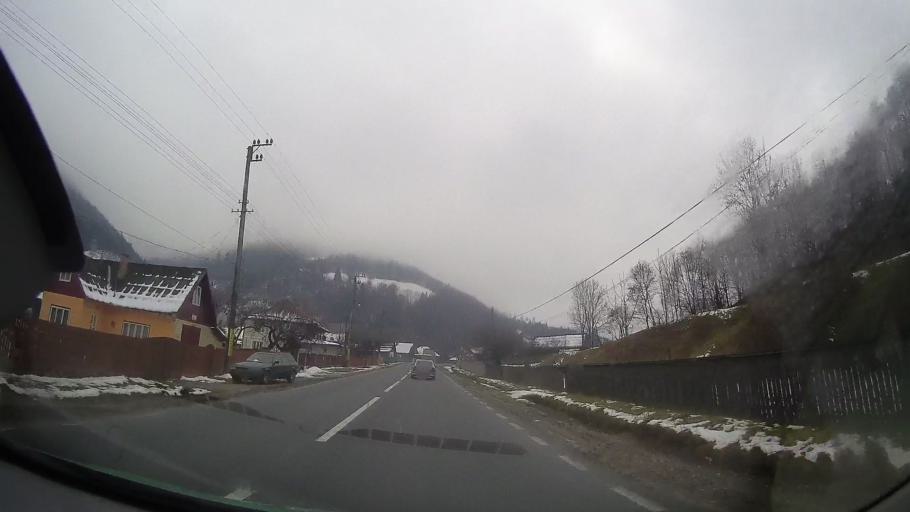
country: RO
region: Neamt
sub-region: Comuna Bicazu Ardelean
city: Bicazu Ardelean
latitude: 46.8551
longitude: 25.9355
